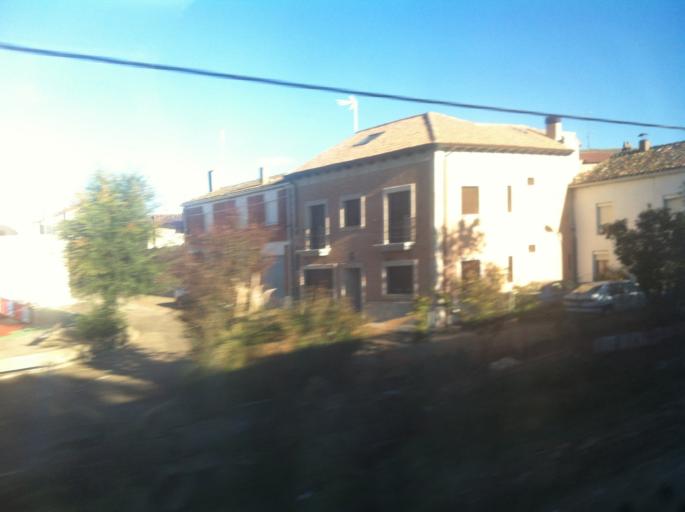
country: ES
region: Castille and Leon
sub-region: Provincia de Palencia
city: Soto de Cerrato
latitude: 41.9827
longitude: -4.4256
